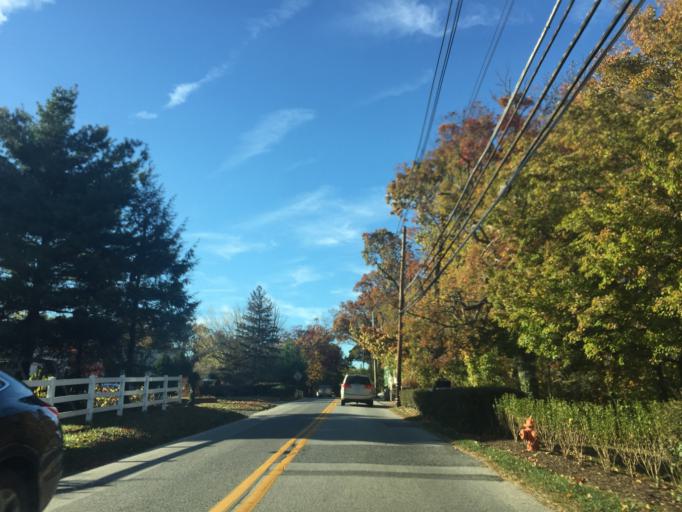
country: US
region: Maryland
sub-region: Baltimore County
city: Lutherville
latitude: 39.4079
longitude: -76.6179
